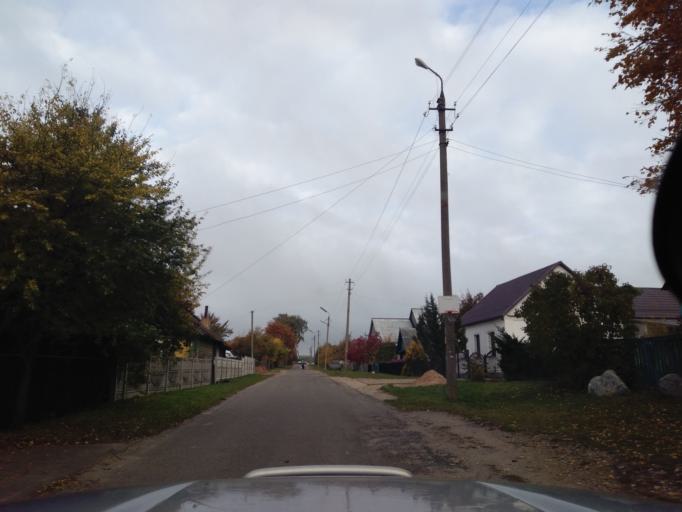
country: BY
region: Minsk
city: Kapyl'
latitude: 53.1584
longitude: 27.0839
